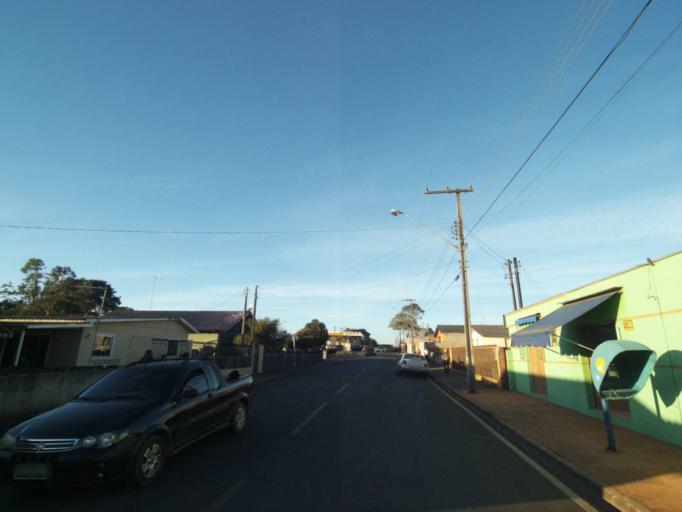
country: BR
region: Parana
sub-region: Tibagi
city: Tibagi
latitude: -24.5115
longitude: -50.4149
